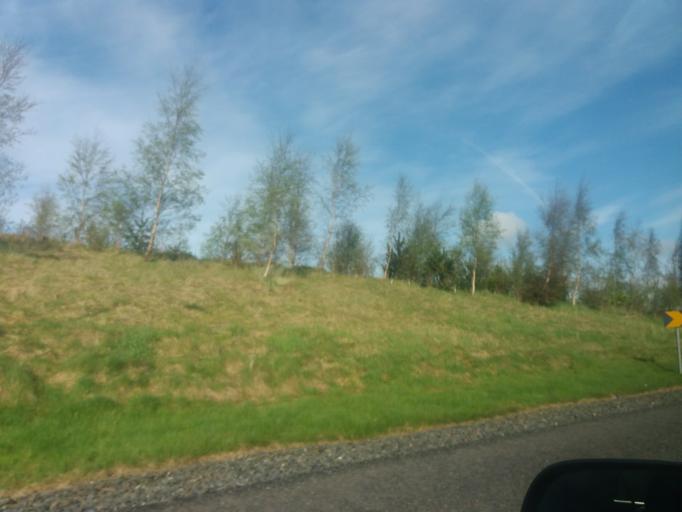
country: IE
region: Leinster
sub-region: An Mhi
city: Kells
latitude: 53.7071
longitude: -6.8578
